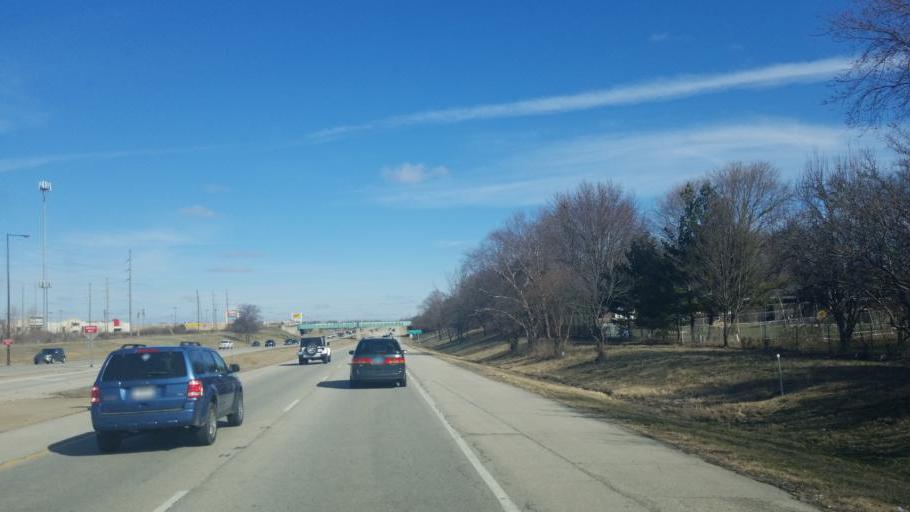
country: US
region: Illinois
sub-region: Sangamon County
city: Jerome
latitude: 39.7530
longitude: -89.7060
